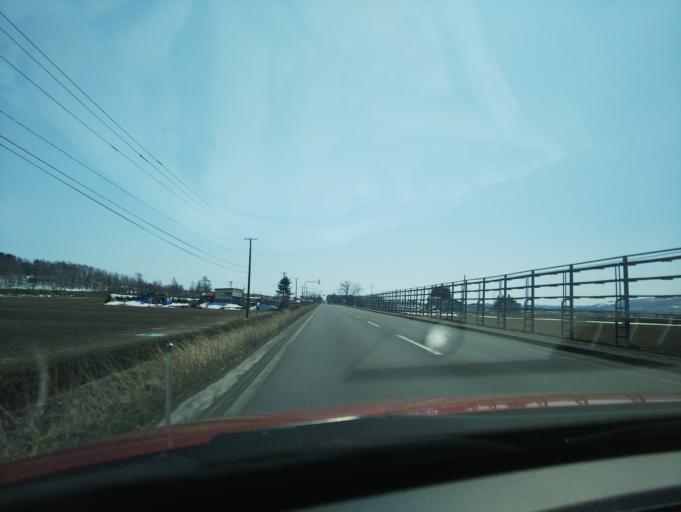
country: JP
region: Hokkaido
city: Nayoro
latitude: 44.2635
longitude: 142.3946
